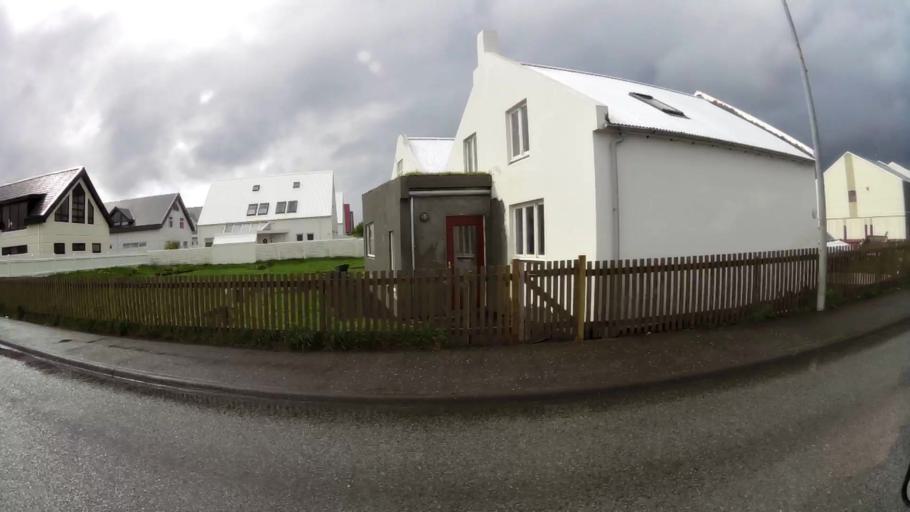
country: IS
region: Capital Region
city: Seltjarnarnes
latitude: 64.1589
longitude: -21.9967
